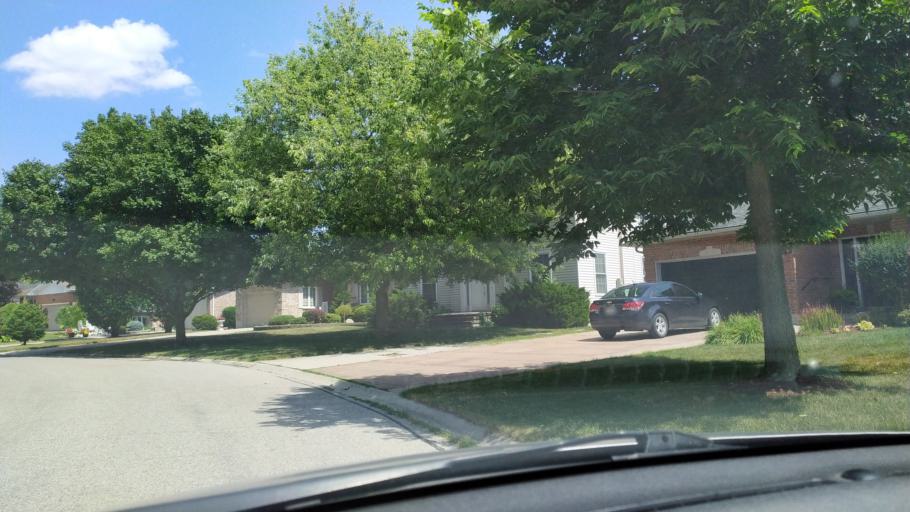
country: CA
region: Ontario
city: Stratford
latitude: 43.3664
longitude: -81.0001
